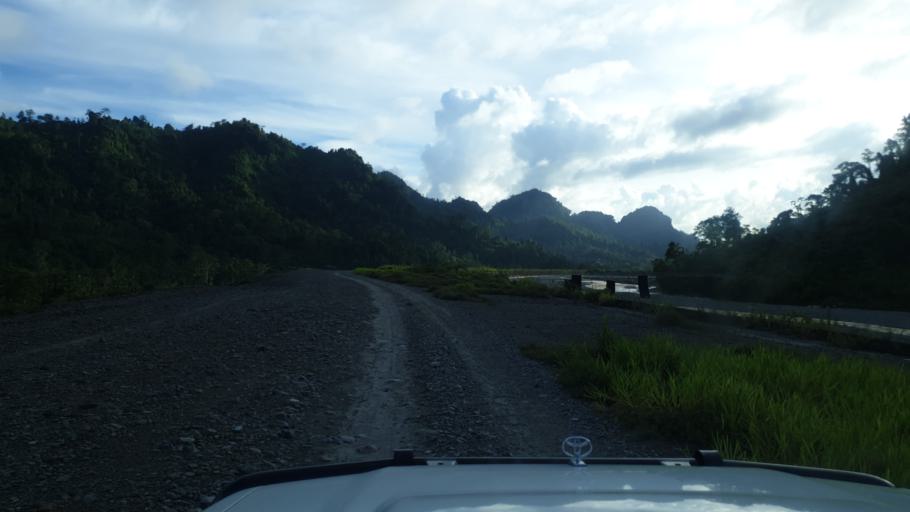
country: PG
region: Bougainville
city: Panguna
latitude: -6.3790
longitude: 155.4321
